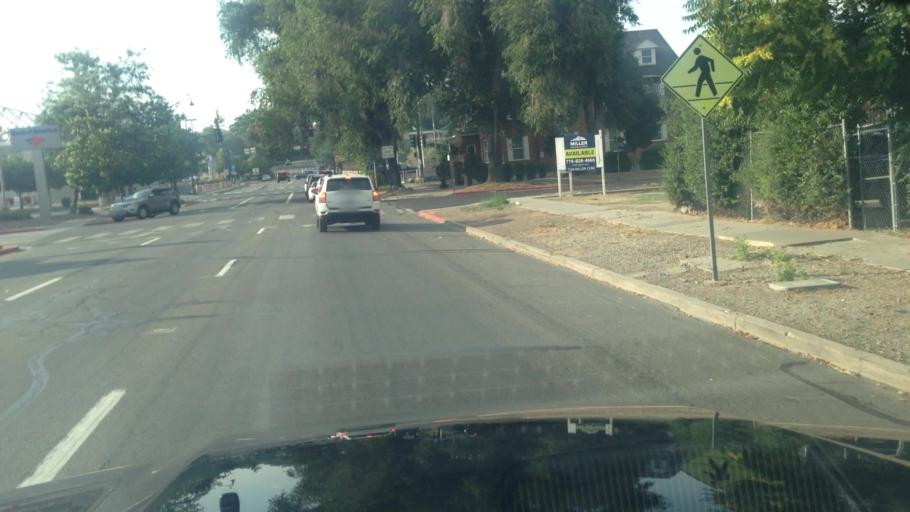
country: US
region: Nevada
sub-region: Washoe County
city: Reno
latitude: 39.5336
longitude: -119.8140
